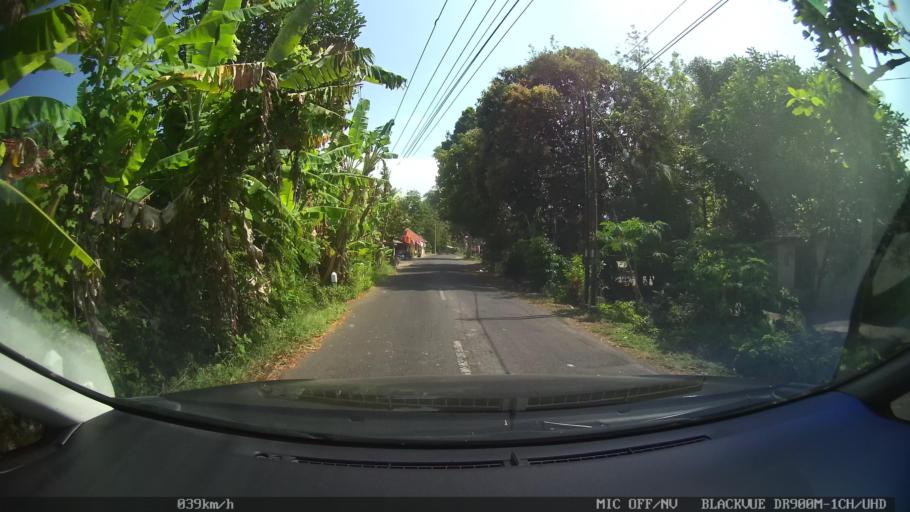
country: ID
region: Daerah Istimewa Yogyakarta
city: Srandakan
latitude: -7.9087
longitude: 110.1524
